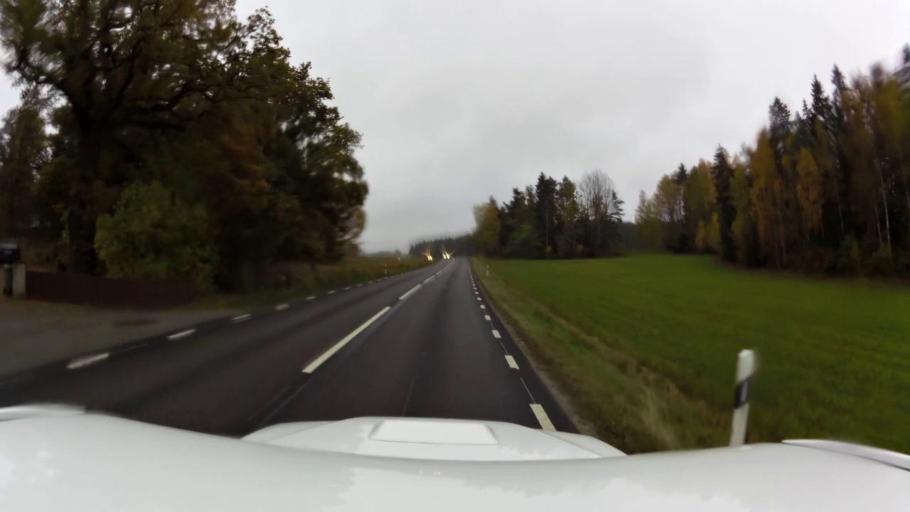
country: SE
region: OEstergoetland
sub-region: Linkopings Kommun
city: Linghem
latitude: 58.3680
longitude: 15.8195
